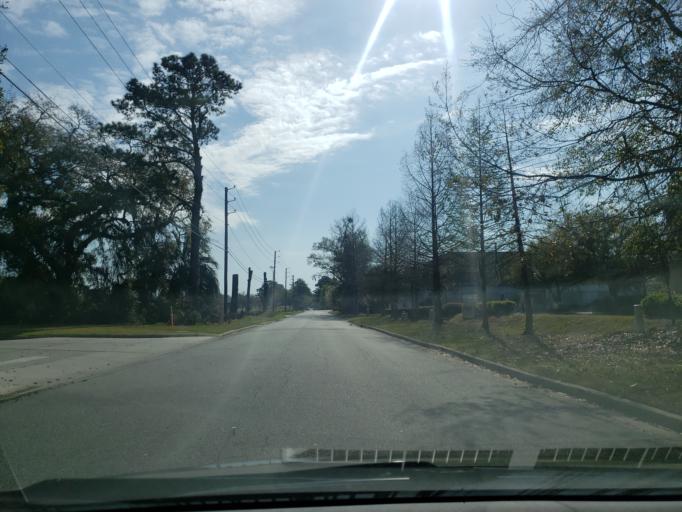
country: US
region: Georgia
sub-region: Chatham County
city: Montgomery
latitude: 32.0010
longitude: -81.1241
